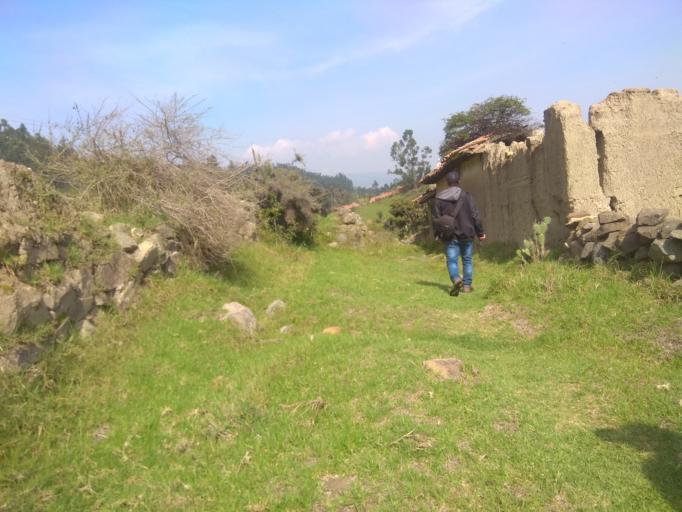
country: CO
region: Boyaca
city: Socha Viejo
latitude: 5.9812
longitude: -72.7080
